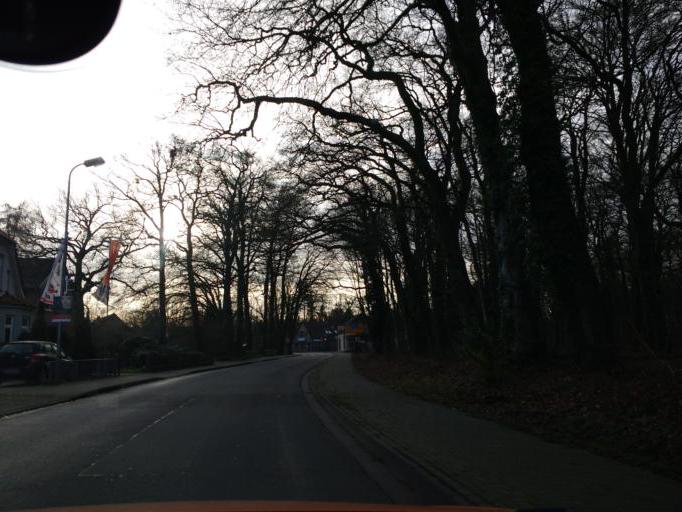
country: DE
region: Lower Saxony
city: Hude
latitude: 53.1171
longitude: 8.4534
